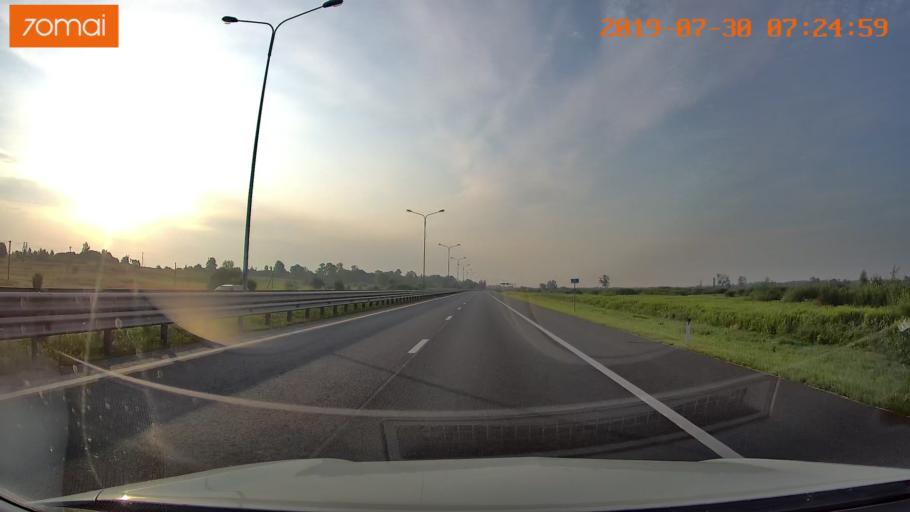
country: RU
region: Kaliningrad
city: Bol'shoe Isakovo
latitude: 54.6898
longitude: 20.8255
